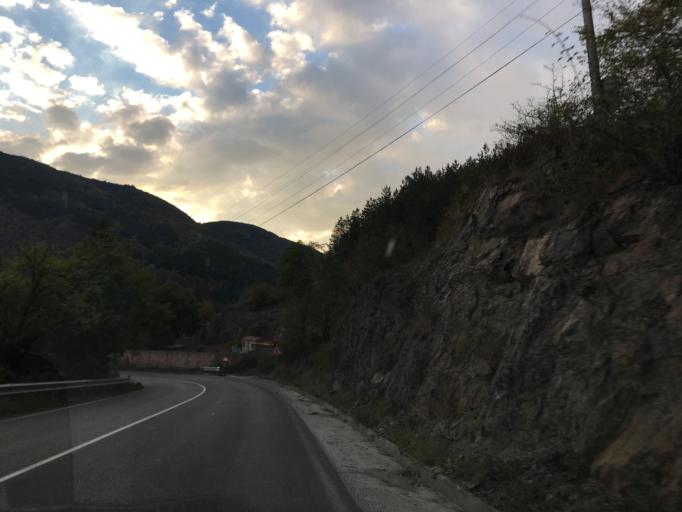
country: BG
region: Sofiya
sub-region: Obshtina Svoge
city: Svoge
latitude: 42.8660
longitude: 23.3595
